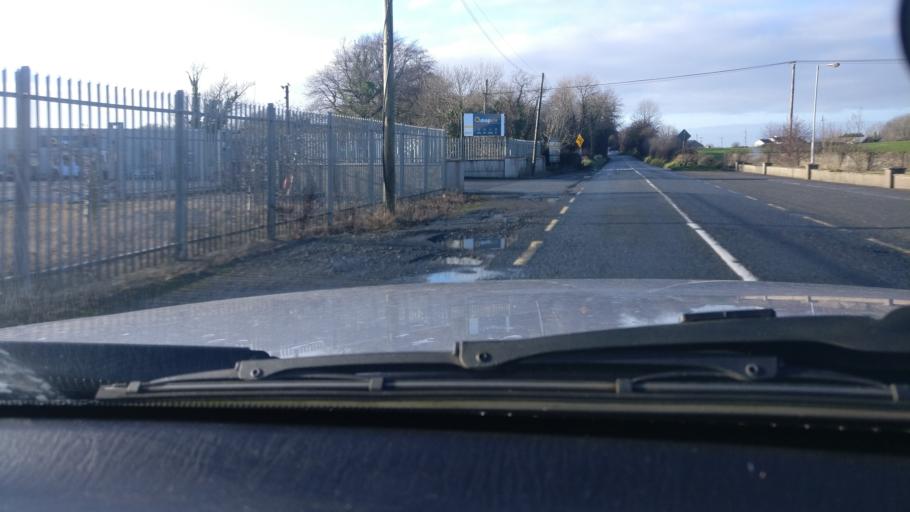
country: IE
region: Leinster
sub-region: An Longfort
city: Ballymahon
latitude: 53.5726
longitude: -7.7514
